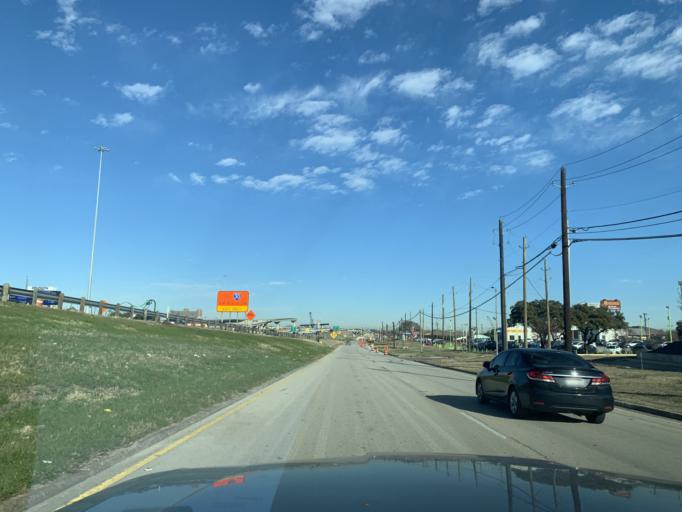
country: US
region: Texas
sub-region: Tarrant County
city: Arlington
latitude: 32.7530
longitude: -97.0625
